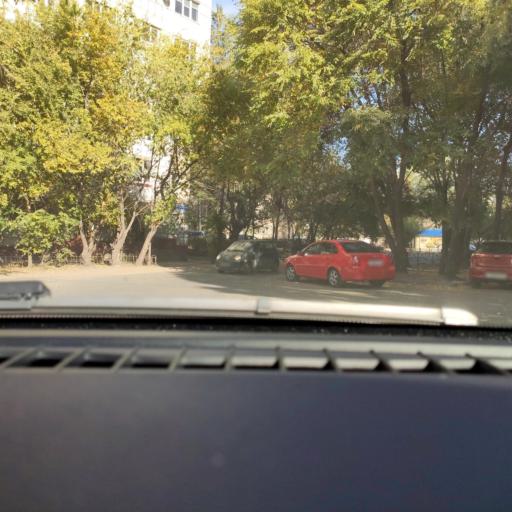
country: RU
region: Voronezj
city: Voronezh
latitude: 51.6689
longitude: 39.2448
